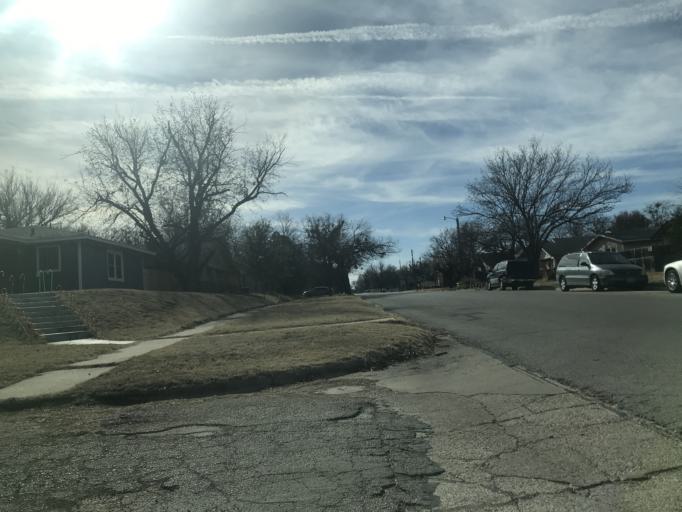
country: US
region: Texas
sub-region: Taylor County
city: Abilene
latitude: 32.4449
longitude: -99.7399
